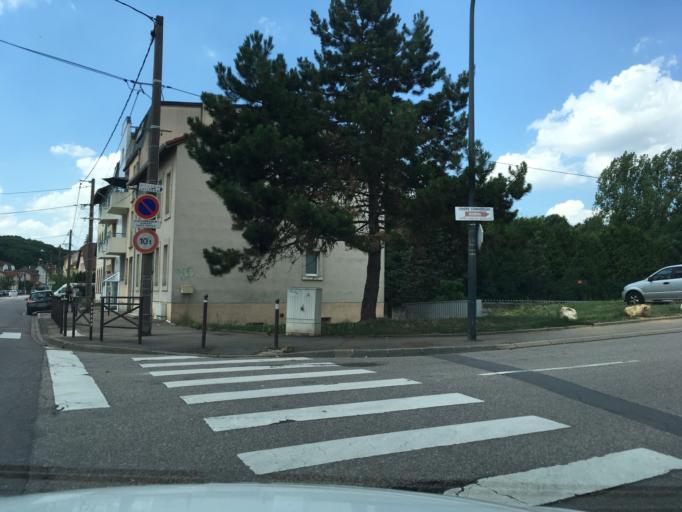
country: FR
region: Lorraine
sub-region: Departement de la Moselle
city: Saint-Julien-les-Metz
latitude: 49.1237
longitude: 6.2033
